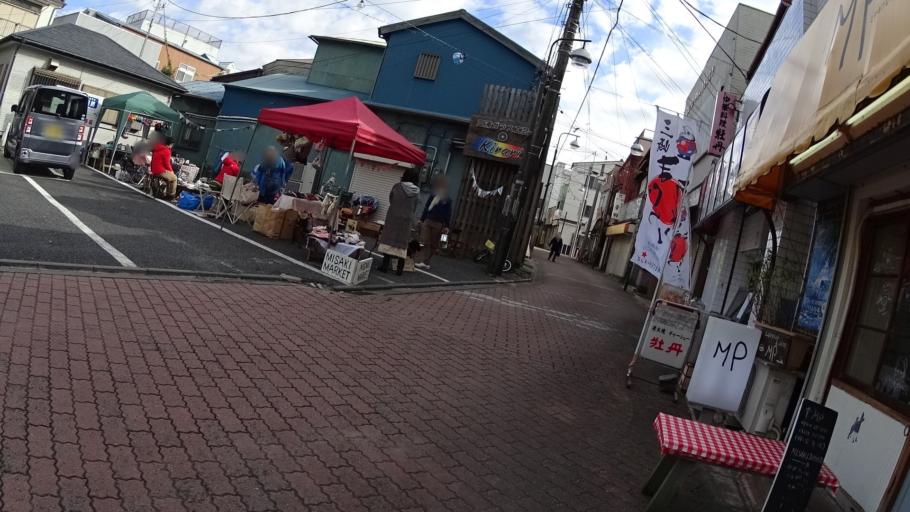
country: JP
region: Kanagawa
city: Miura
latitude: 35.1408
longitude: 139.6187
